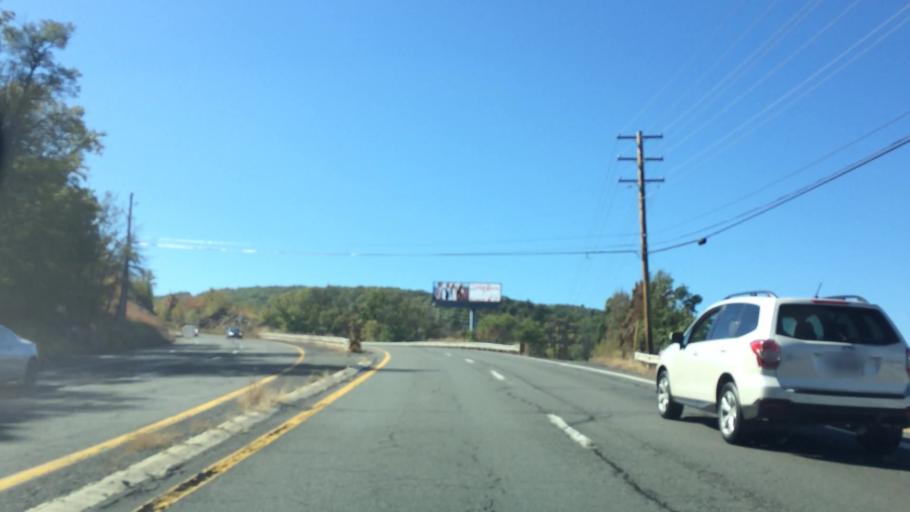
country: US
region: Pennsylvania
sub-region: Luzerne County
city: Ashley
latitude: 41.2056
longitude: -75.8966
